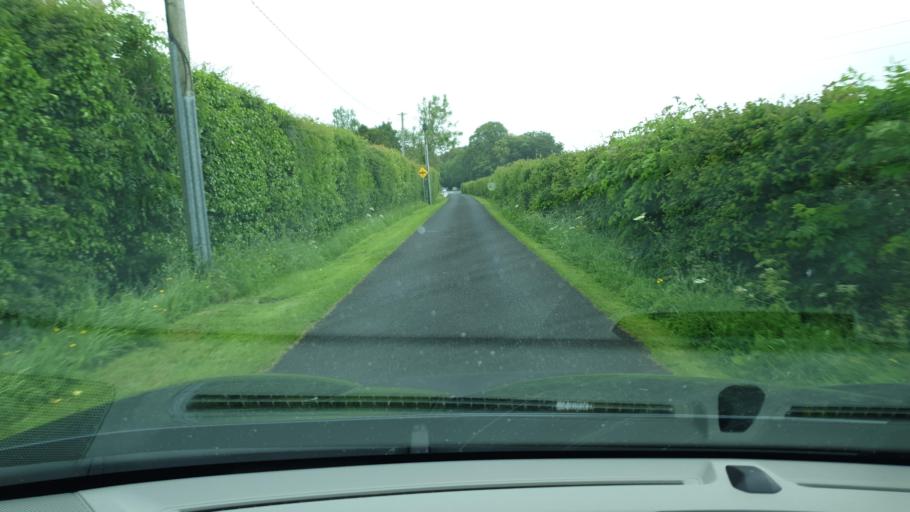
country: IE
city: Confey
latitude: 53.4355
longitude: -6.5273
